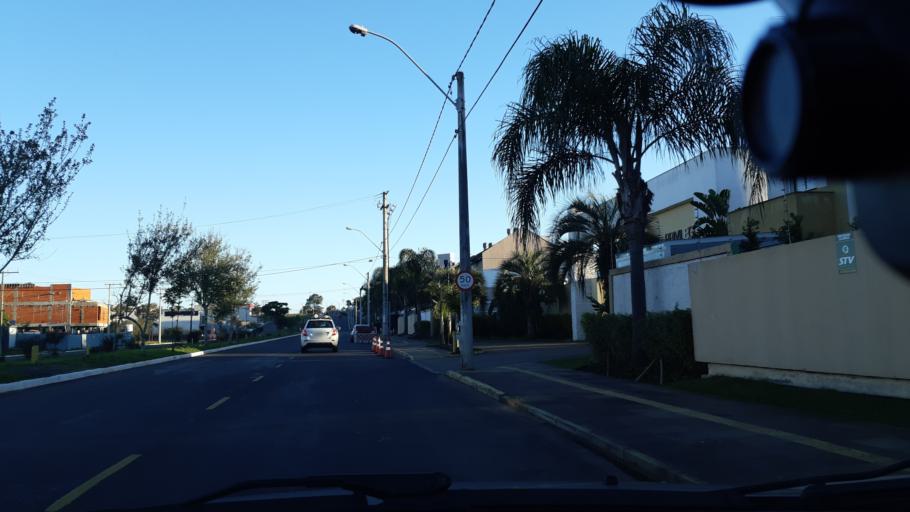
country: BR
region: Rio Grande do Sul
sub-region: Canoas
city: Canoas
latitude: -29.9227
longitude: -51.1556
